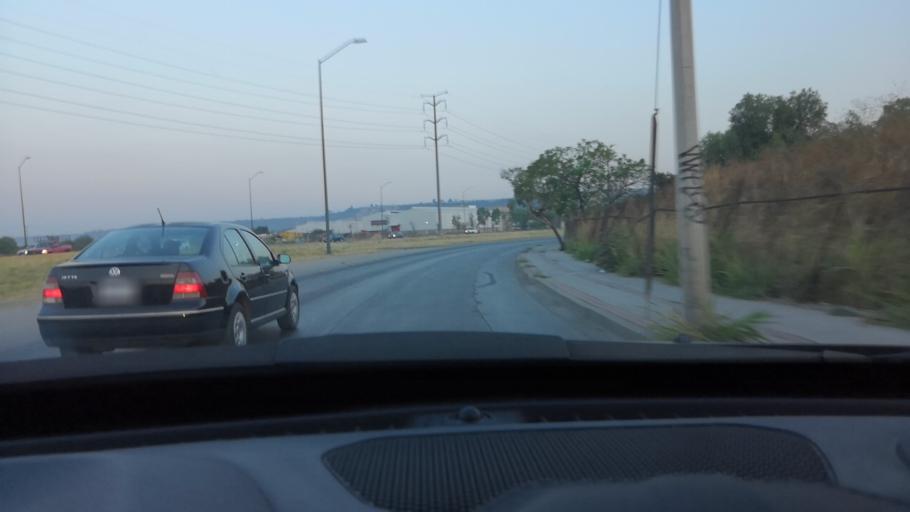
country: MX
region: Guanajuato
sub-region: Leon
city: San Jose de Duran (Los Troncoso)
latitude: 21.0960
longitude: -101.7046
